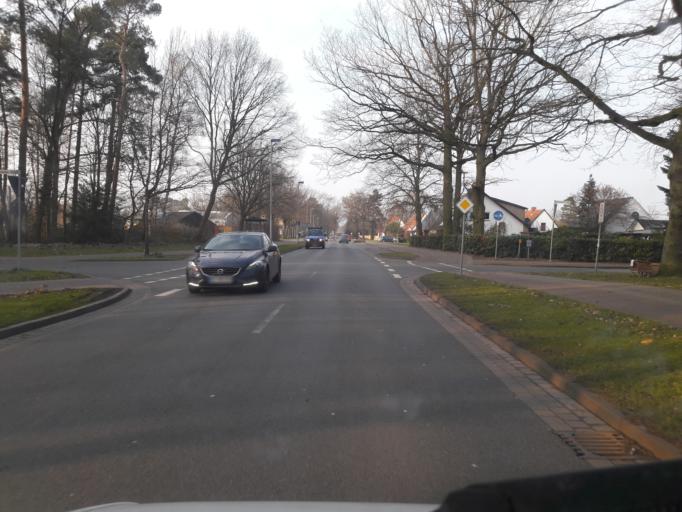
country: DE
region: North Rhine-Westphalia
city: Espelkamp
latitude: 52.3829
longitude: 8.6300
